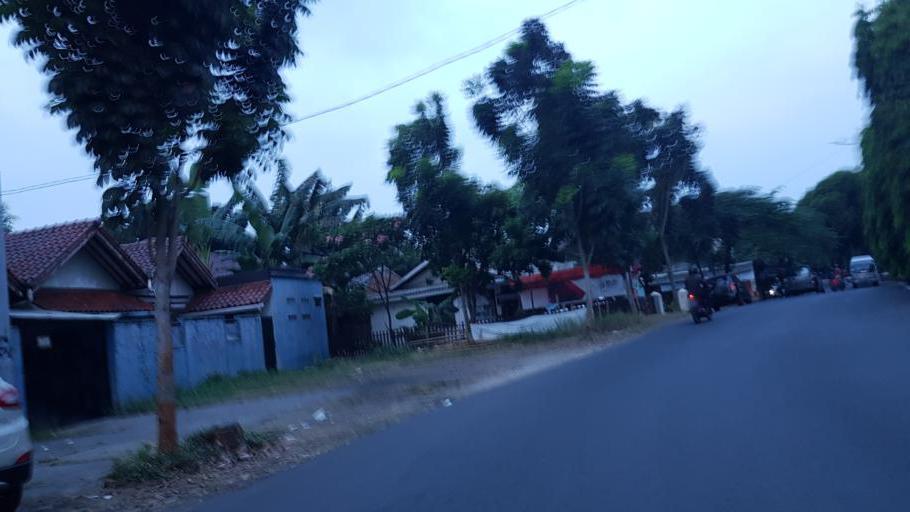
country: ID
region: West Java
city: Pamulang
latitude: -6.3127
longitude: 106.7849
